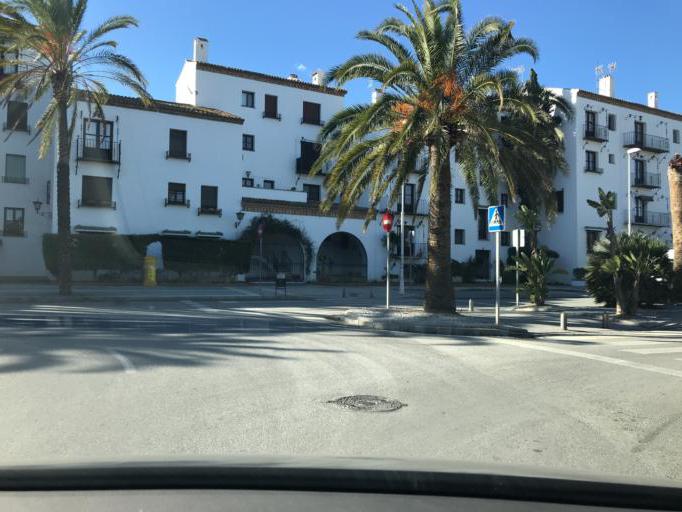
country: ES
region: Andalusia
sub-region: Provincia de Granada
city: Salobrena
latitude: 36.7201
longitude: -3.5601
